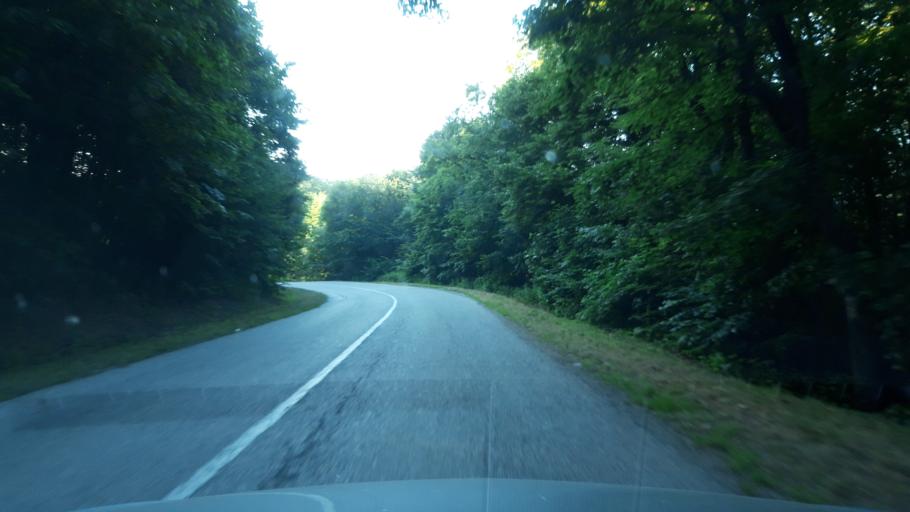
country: RS
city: Glozan
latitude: 45.1512
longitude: 19.5828
